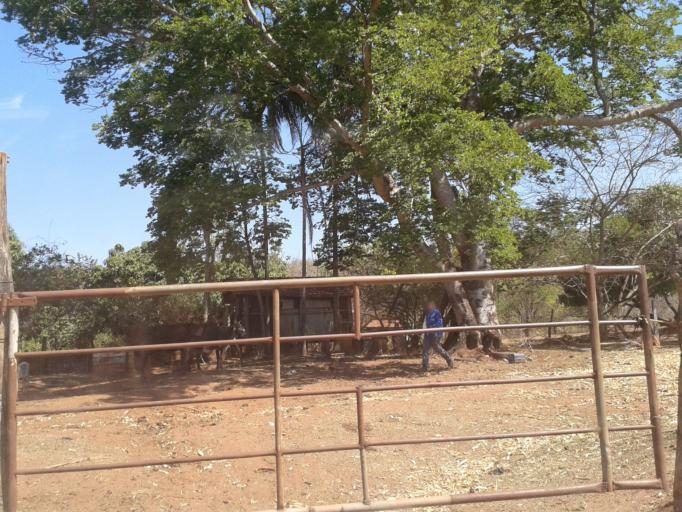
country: BR
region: Minas Gerais
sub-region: Ituiutaba
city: Ituiutaba
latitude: -19.0866
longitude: -49.3024
